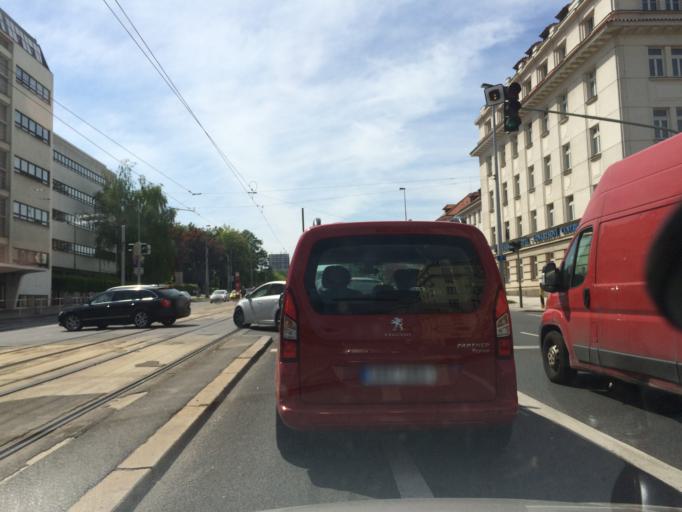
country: CZ
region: Praha
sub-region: Praha 1
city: Mala Strana
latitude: 50.1002
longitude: 14.3875
